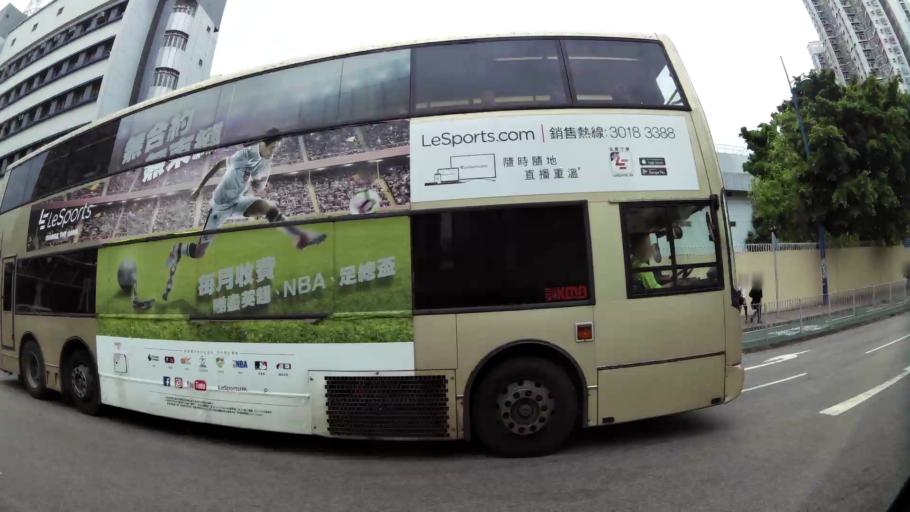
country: HK
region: Yuen Long
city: Yuen Long Kau Hui
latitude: 22.4504
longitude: 114.0024
